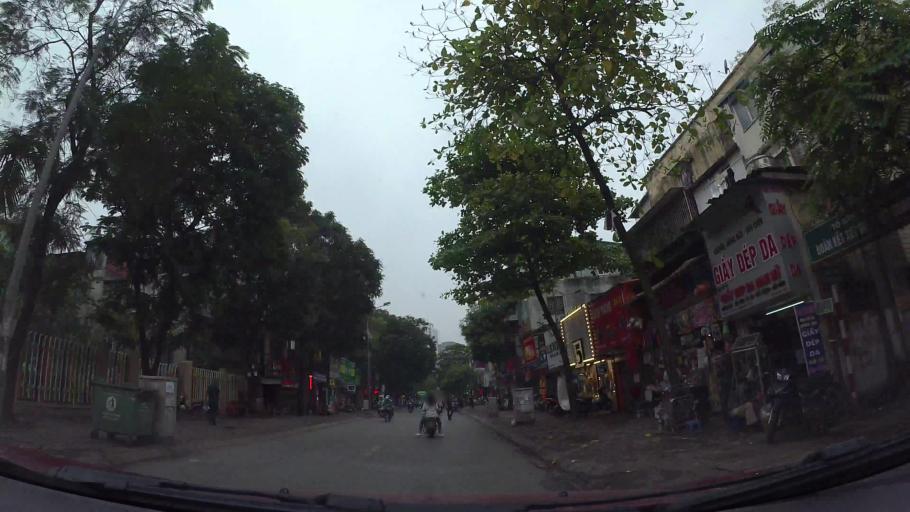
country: VN
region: Ha Noi
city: Hai BaTrung
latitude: 21.0053
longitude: 105.8355
